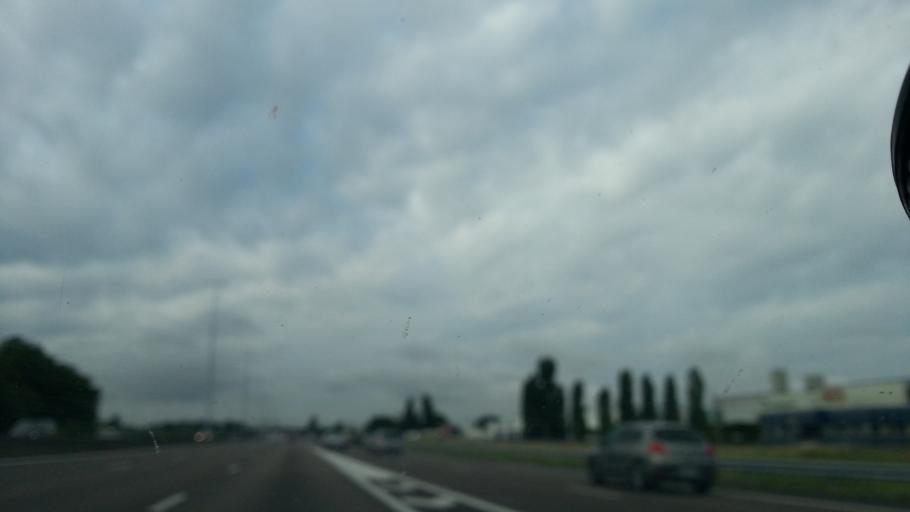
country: FR
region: Bourgogne
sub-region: Departement de la Cote-d'Or
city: Beaune
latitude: 47.0224
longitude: 4.8713
